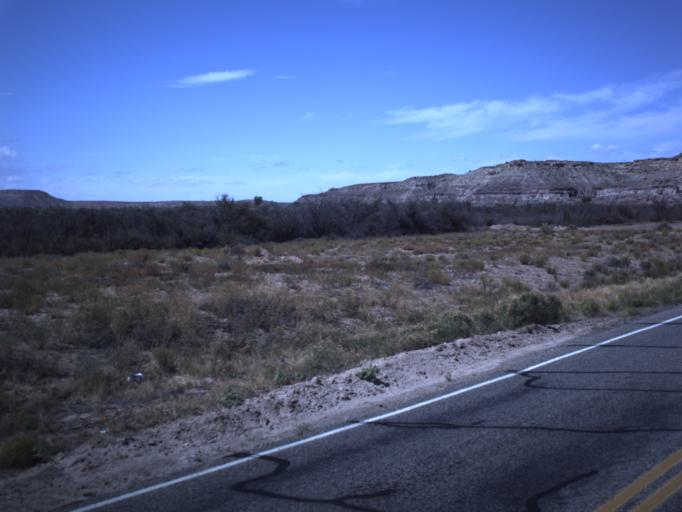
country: US
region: Utah
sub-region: San Juan County
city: Blanding
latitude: 37.2535
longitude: -109.2583
